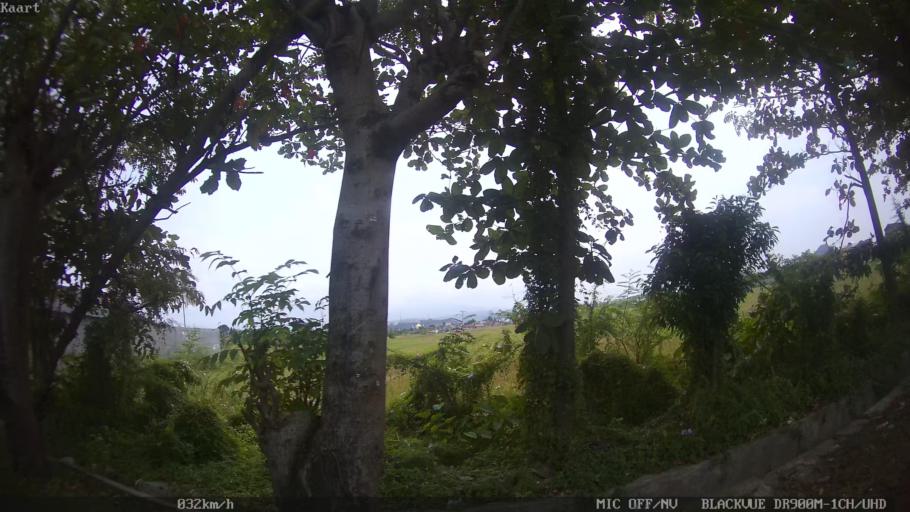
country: ID
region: Lampung
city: Bandarlampung
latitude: -5.4068
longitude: 105.2854
